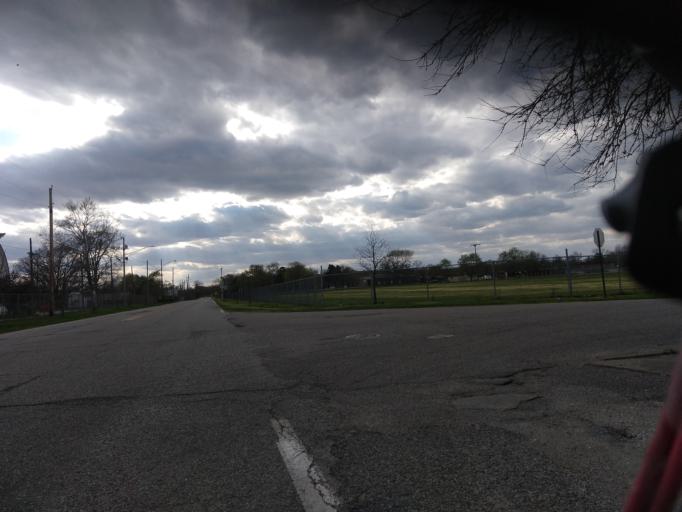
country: US
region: Indiana
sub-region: Marion County
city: Broad Ripple
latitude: 39.8329
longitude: -86.1312
